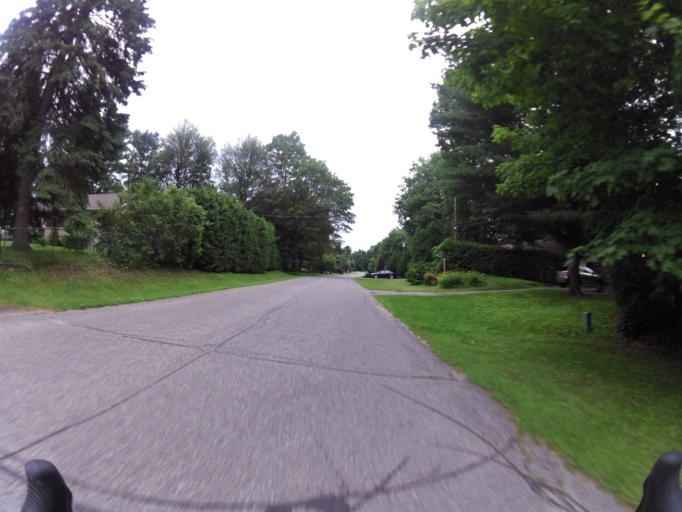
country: CA
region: Ontario
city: Ottawa
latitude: 45.3185
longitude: -75.7208
